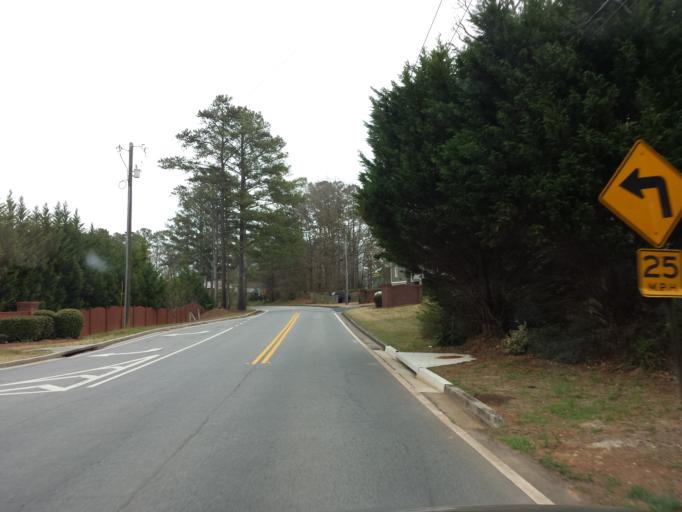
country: US
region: Georgia
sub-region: Cherokee County
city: Woodstock
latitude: 34.0457
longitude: -84.5086
